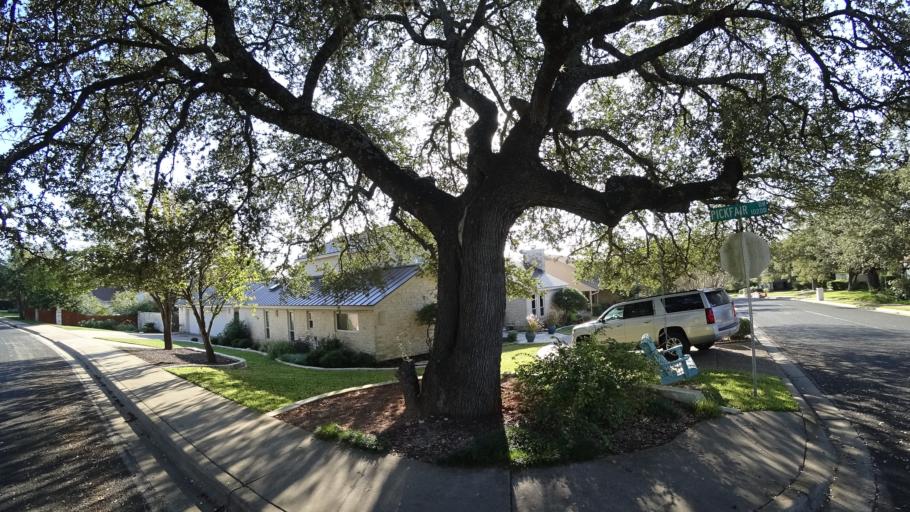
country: US
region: Texas
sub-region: Williamson County
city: Anderson Mill
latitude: 30.4298
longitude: -97.8108
